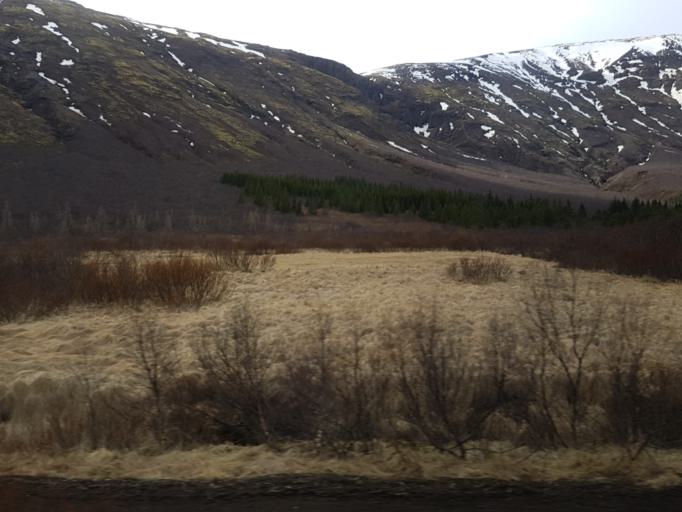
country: IS
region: South
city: Selfoss
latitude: 64.2235
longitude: -20.7262
